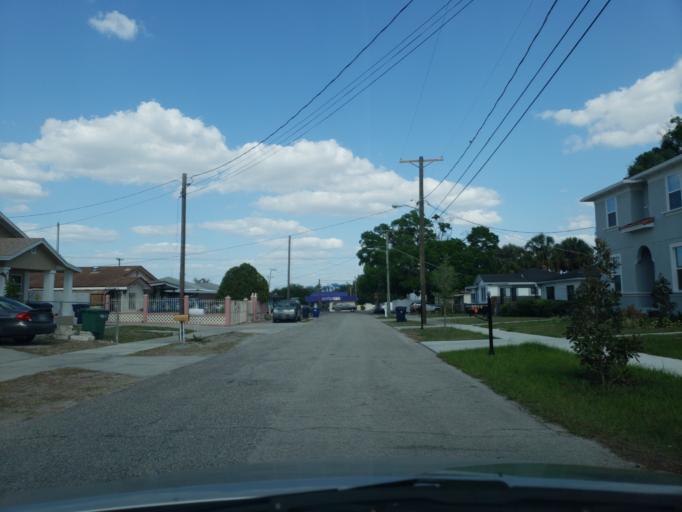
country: US
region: Florida
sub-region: Hillsborough County
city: Tampa
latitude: 27.9733
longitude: -82.4859
